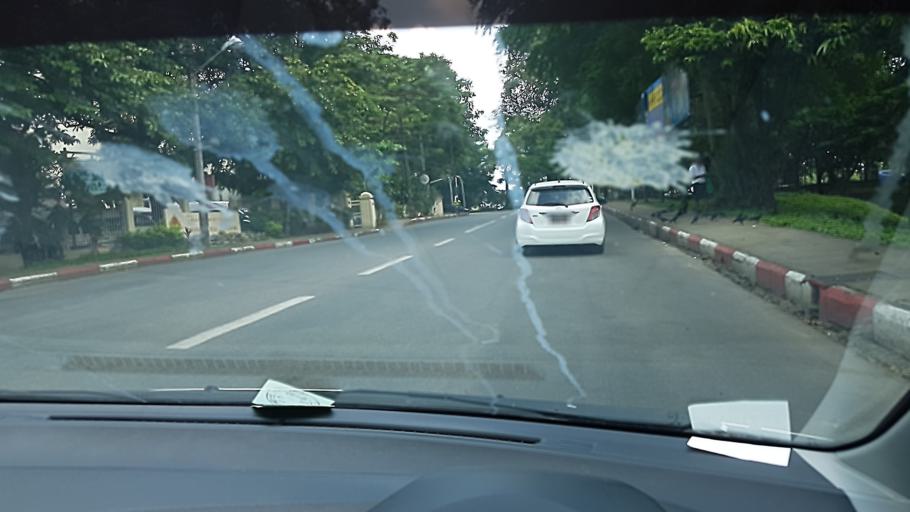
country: MM
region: Yangon
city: Yangon
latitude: 16.7917
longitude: 96.1670
